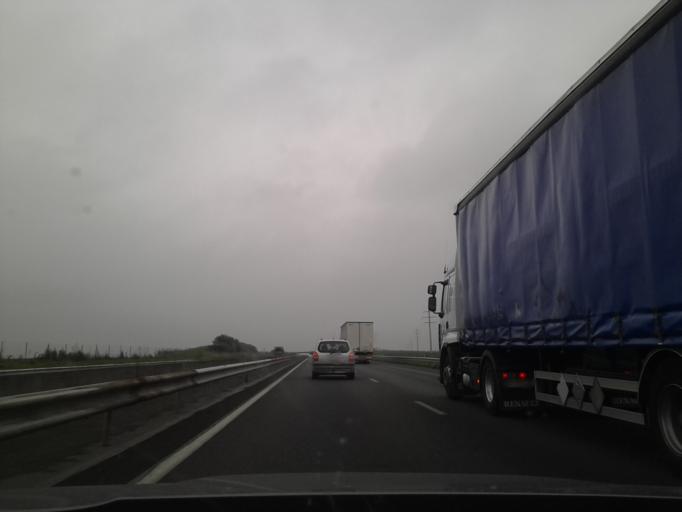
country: FR
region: Nord-Pas-de-Calais
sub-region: Departement du Nord
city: Iwuy
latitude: 50.2384
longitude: 3.2919
